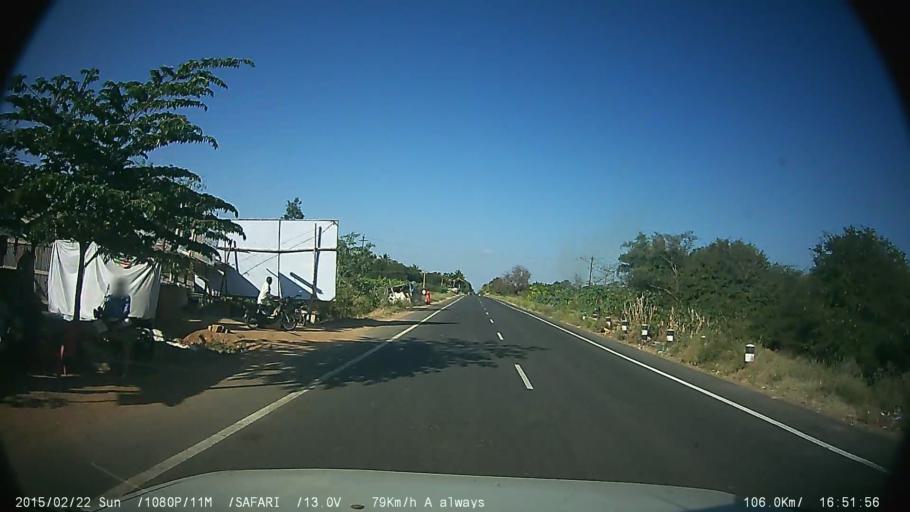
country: IN
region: Tamil Nadu
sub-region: Theni
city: Gudalur
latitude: 9.6536
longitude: 77.2209
